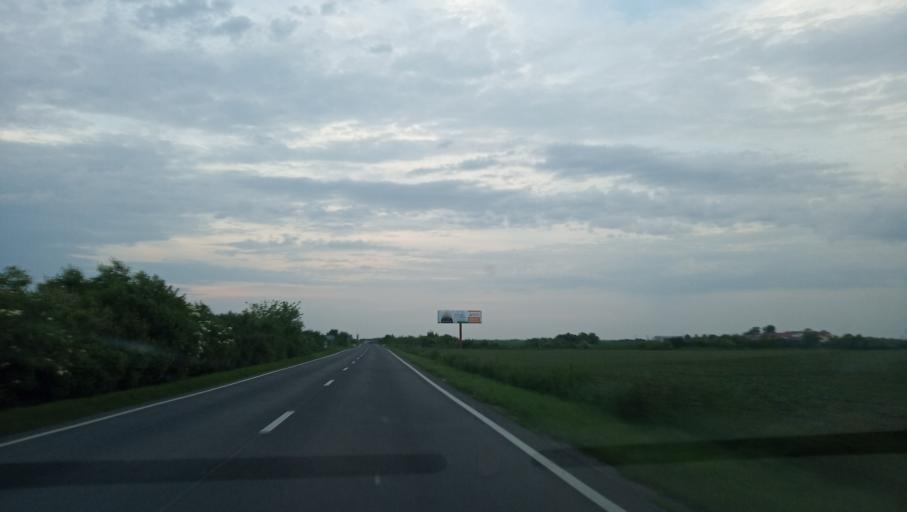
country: RO
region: Timis
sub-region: Comuna Voiteg
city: Voiteg
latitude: 45.4886
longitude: 21.2346
